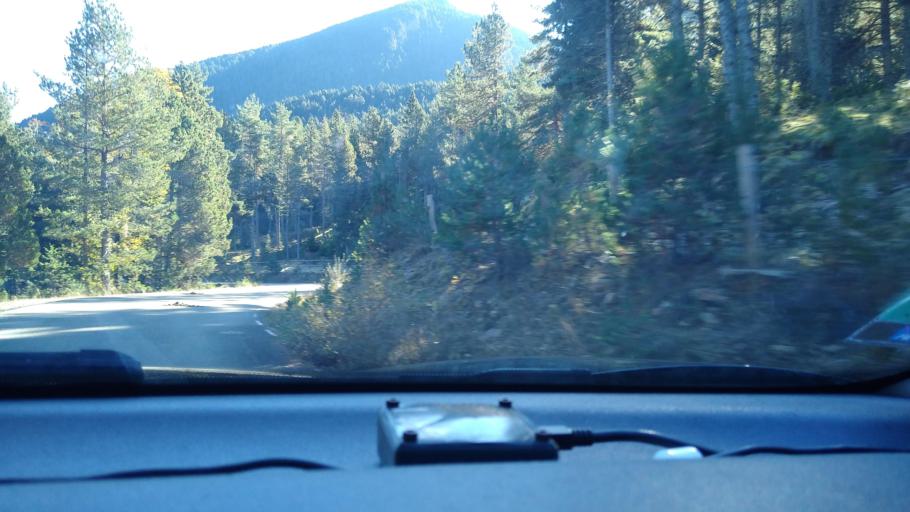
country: ES
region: Catalonia
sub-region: Provincia de Barcelona
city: Saldes
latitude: 42.1987
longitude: 1.7549
